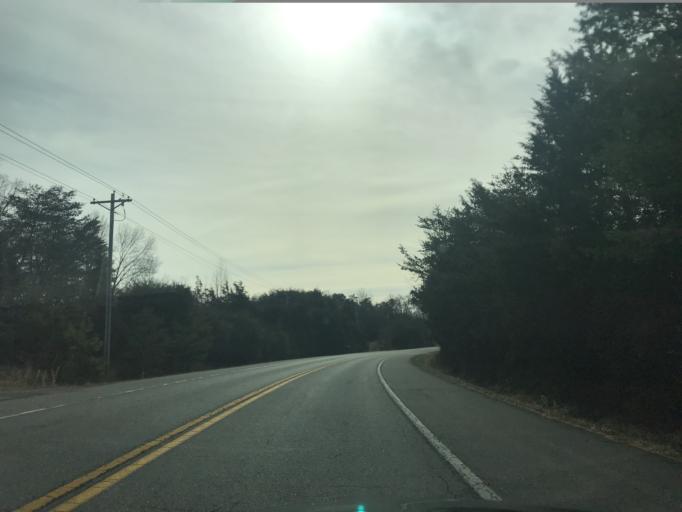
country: US
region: Virginia
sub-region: Prince William County
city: Cherry Hill
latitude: 38.4765
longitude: -77.2263
